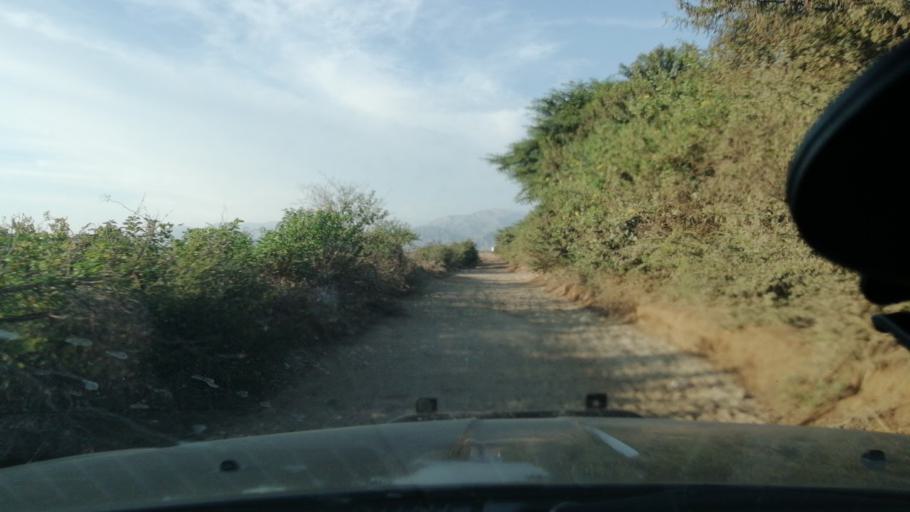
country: PE
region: Ica
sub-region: Provincia de Chincha
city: San Pedro
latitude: -13.3420
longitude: -76.1589
